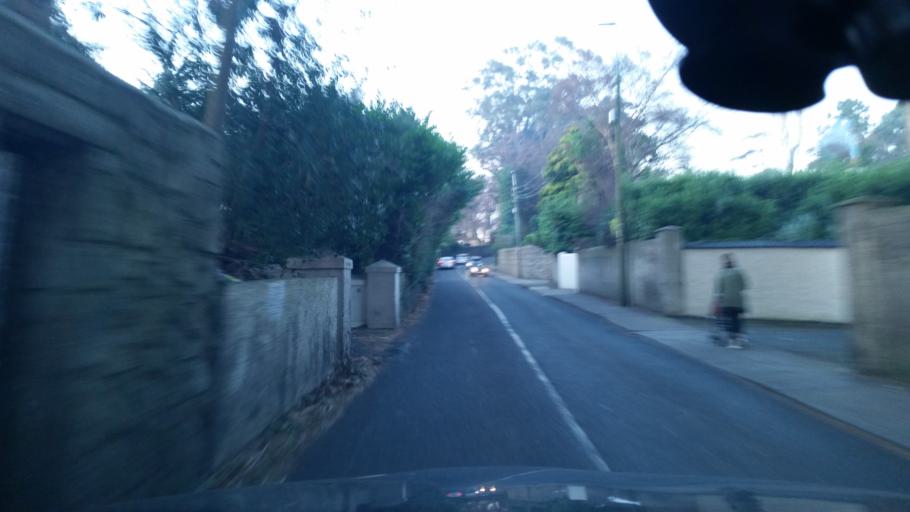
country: IE
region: Leinster
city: Loughlinstown
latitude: 53.2493
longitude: -6.1200
